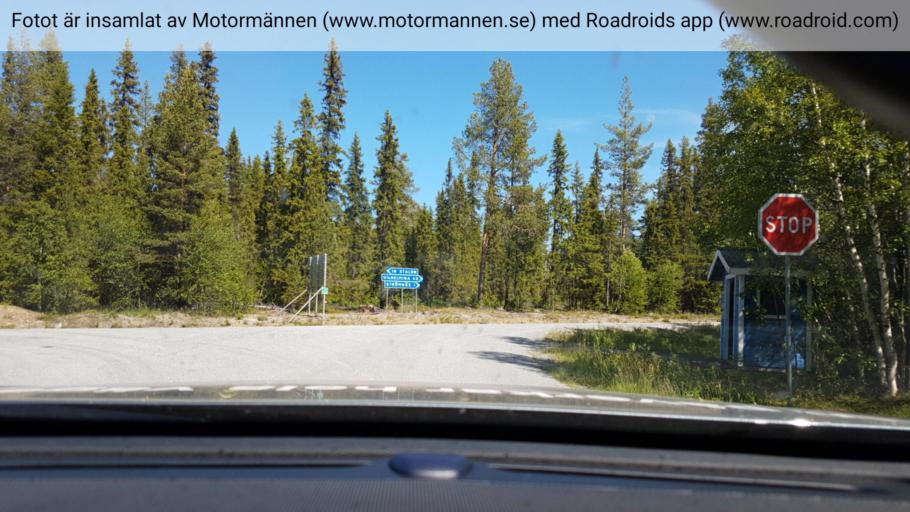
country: SE
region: Vaesterbotten
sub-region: Vilhelmina Kommun
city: Sjoberg
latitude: 64.8020
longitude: 16.0074
